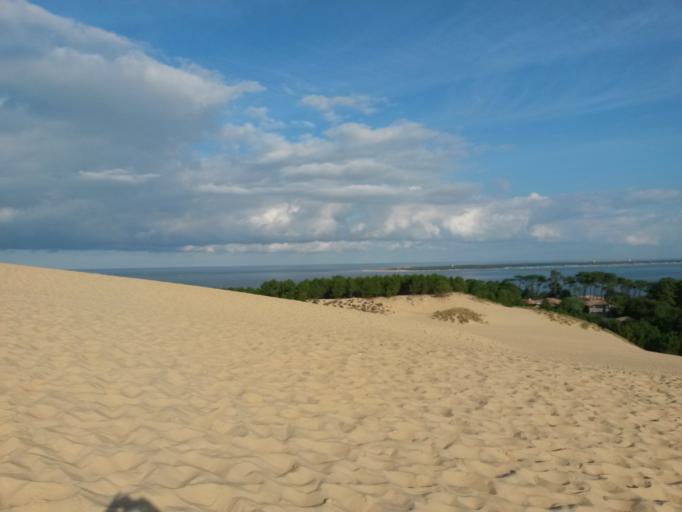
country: FR
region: Aquitaine
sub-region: Departement de la Gironde
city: Arcachon
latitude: 44.5990
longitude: -1.2053
